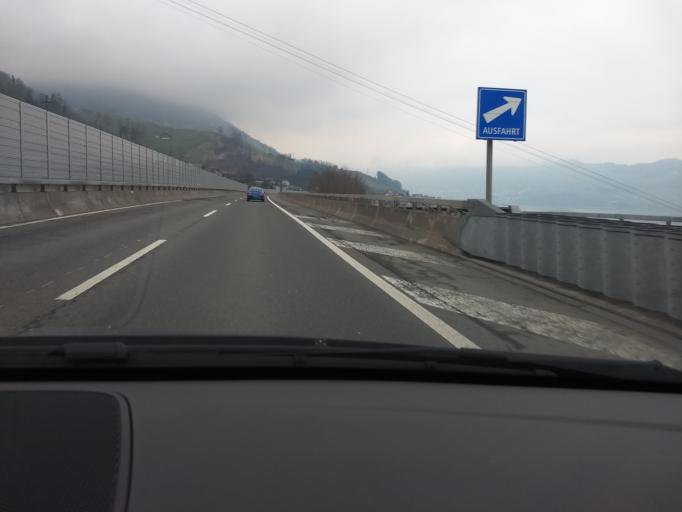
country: CH
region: Nidwalden
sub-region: Nidwalden
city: Beckenried
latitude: 46.9625
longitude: 8.4757
